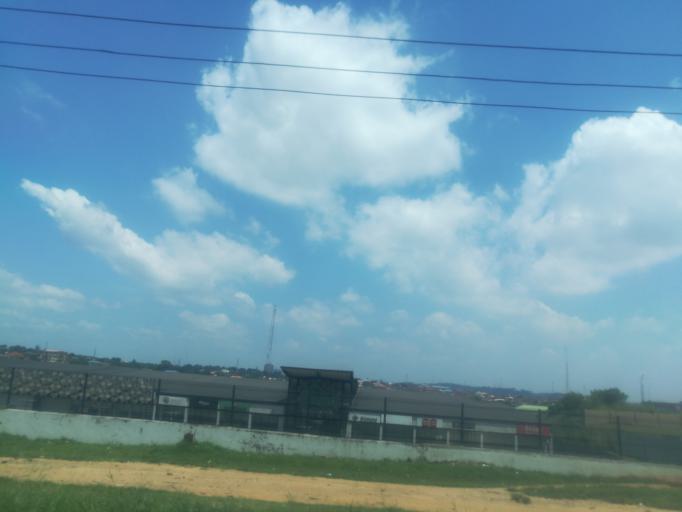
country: NG
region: Oyo
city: Ibadan
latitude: 7.3628
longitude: 3.8656
